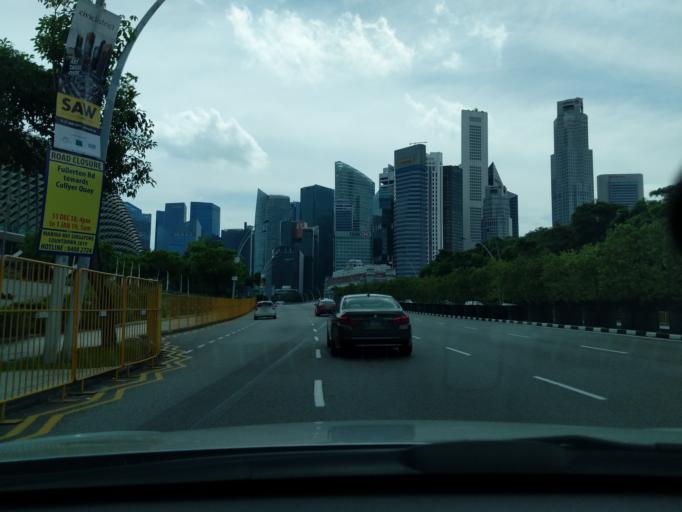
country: SG
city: Singapore
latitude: 1.2898
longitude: 103.8547
